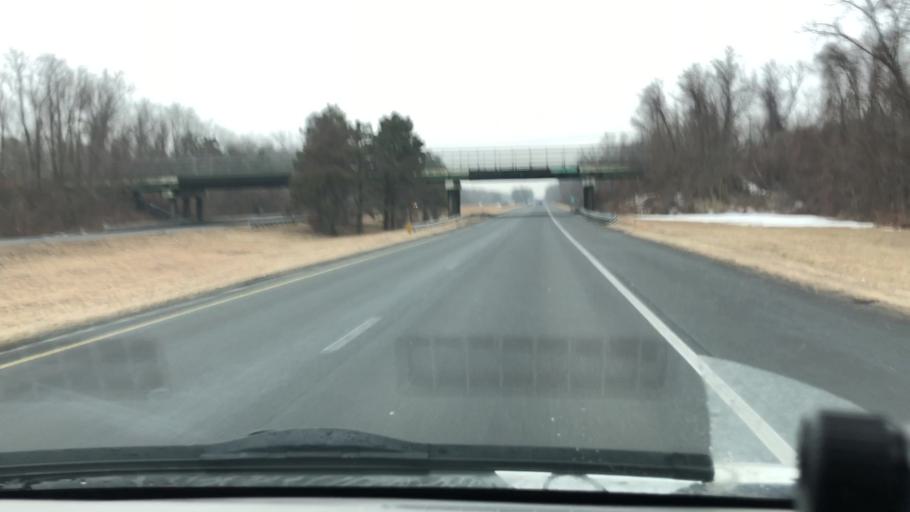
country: US
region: Massachusetts
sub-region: Franklin County
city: Whately
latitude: 42.4122
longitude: -72.6261
